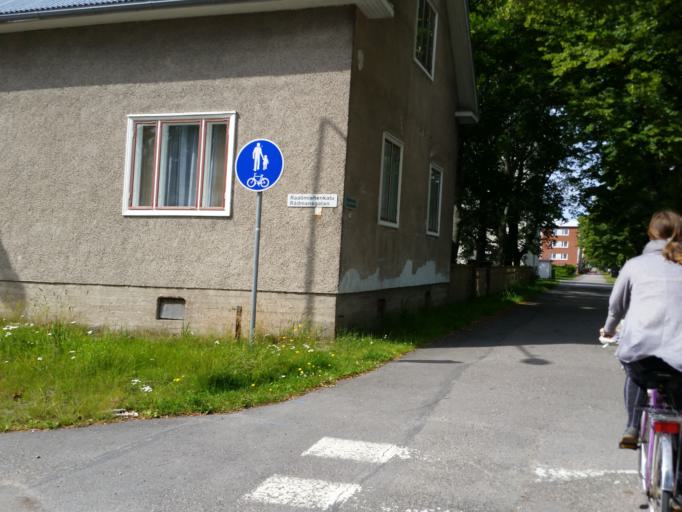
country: FI
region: Uusimaa
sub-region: Raaseporin
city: Hanko
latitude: 59.8284
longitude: 22.9631
